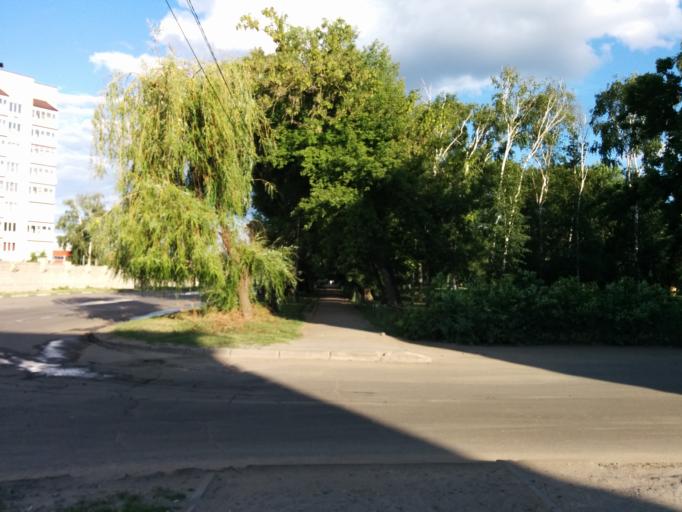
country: RU
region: Tambov
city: Tambov
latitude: 52.7456
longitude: 41.4441
